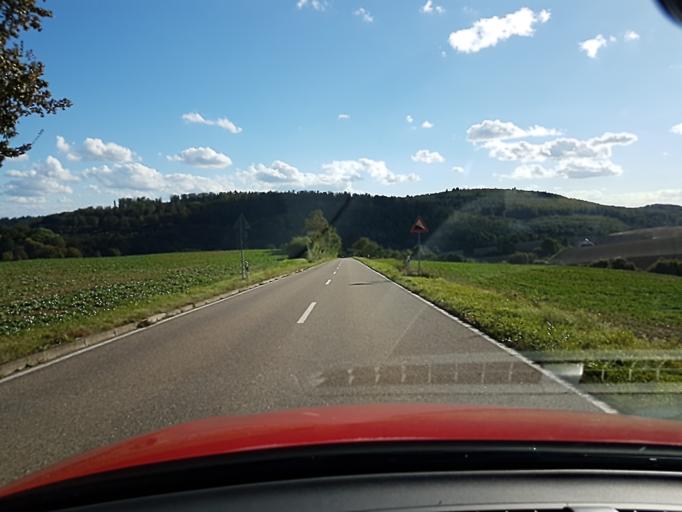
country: DE
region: Baden-Wuerttemberg
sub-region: Karlsruhe Region
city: Wiesenbach
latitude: 49.3694
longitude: 8.8383
